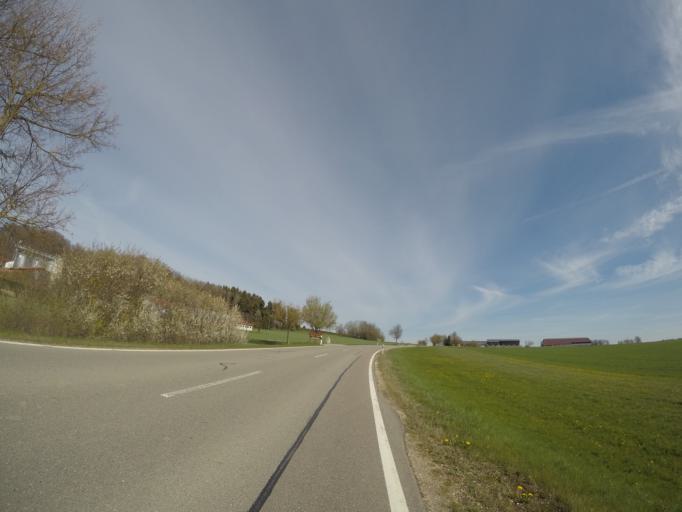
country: DE
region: Baden-Wuerttemberg
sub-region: Tuebingen Region
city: Laichingen
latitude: 48.5066
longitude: 9.6732
